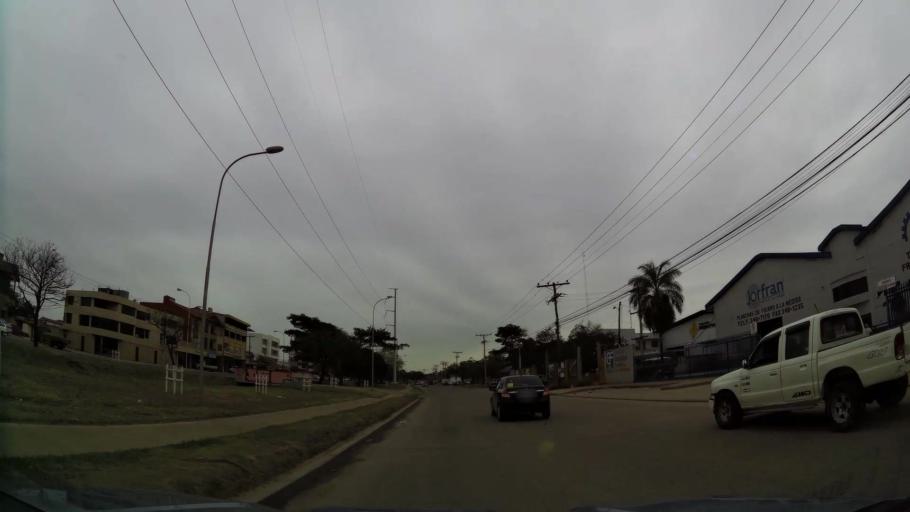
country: BO
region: Santa Cruz
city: Santa Cruz de la Sierra
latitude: -17.7593
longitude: -63.1523
